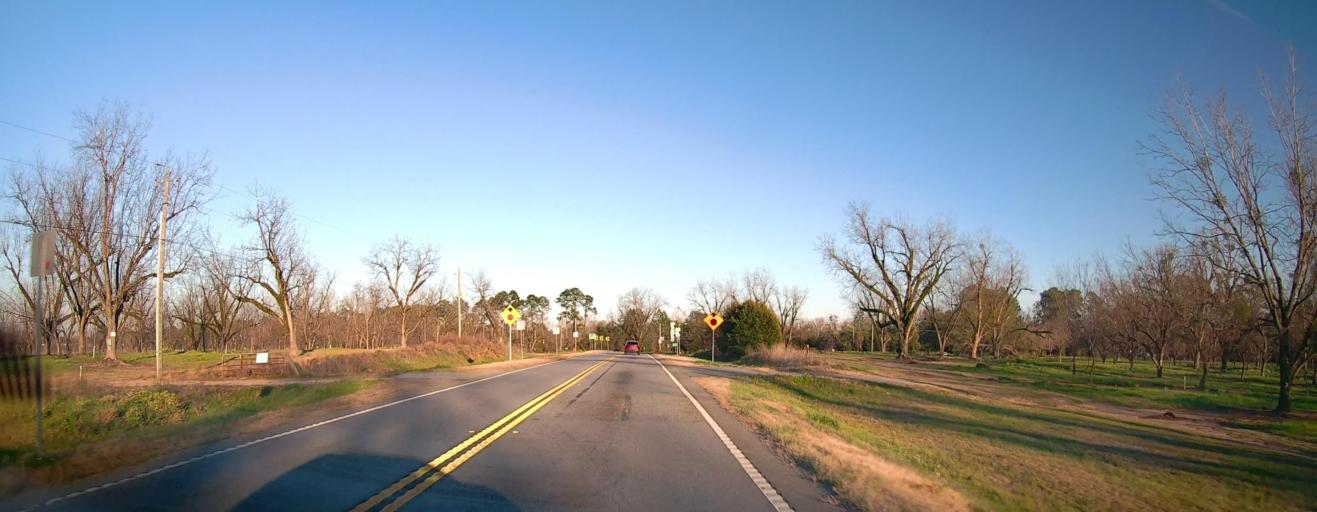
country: US
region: Georgia
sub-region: Dougherty County
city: Albany
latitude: 31.5041
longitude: -84.2133
